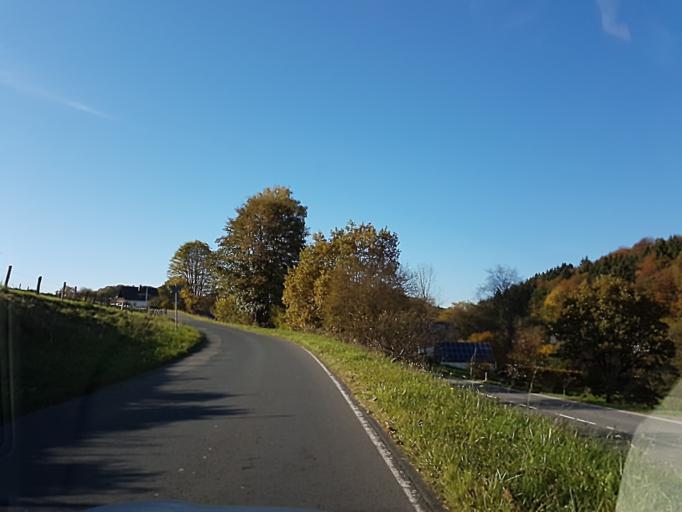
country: DE
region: North Rhine-Westphalia
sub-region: Regierungsbezirk Arnsberg
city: Drolshagen
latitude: 51.0667
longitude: 7.7223
